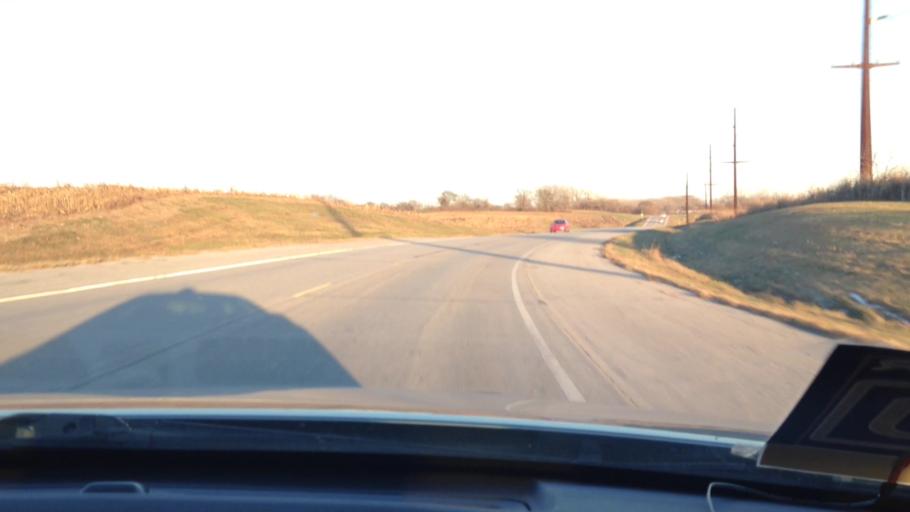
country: US
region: Missouri
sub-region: Platte County
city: Platte City
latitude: 39.3395
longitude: -94.7482
